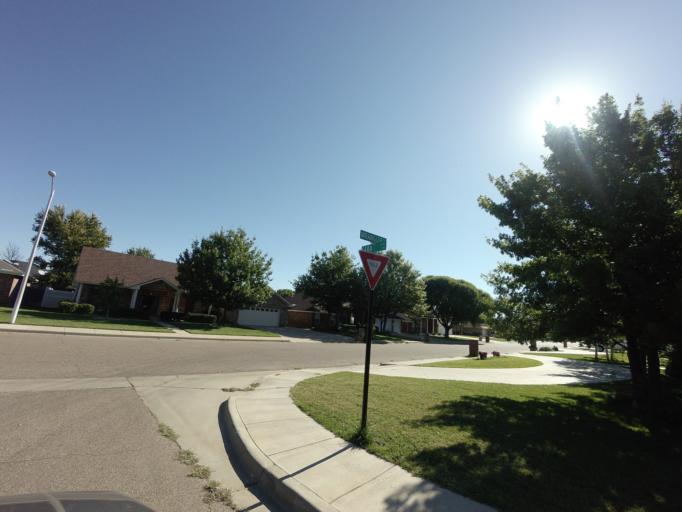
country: US
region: New Mexico
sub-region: Curry County
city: Clovis
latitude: 34.4251
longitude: -103.1717
